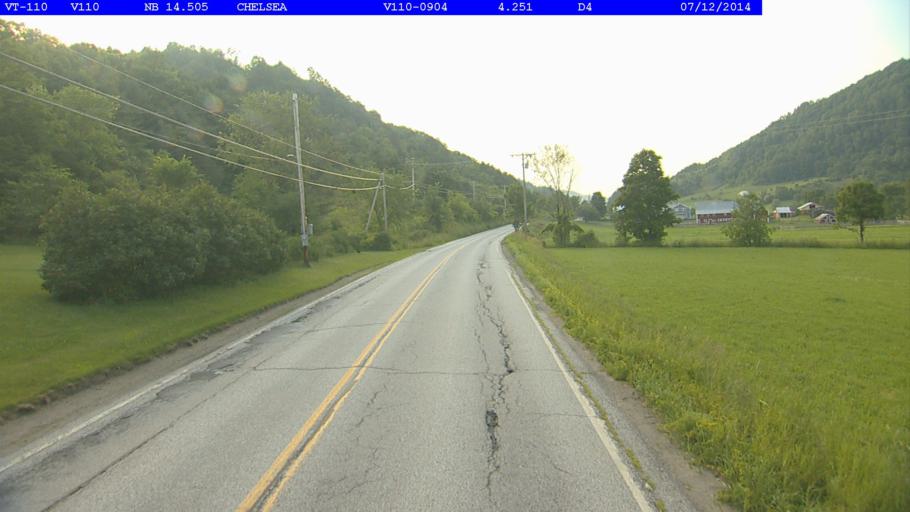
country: US
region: Vermont
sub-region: Orange County
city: Chelsea
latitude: 44.0044
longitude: -72.4582
